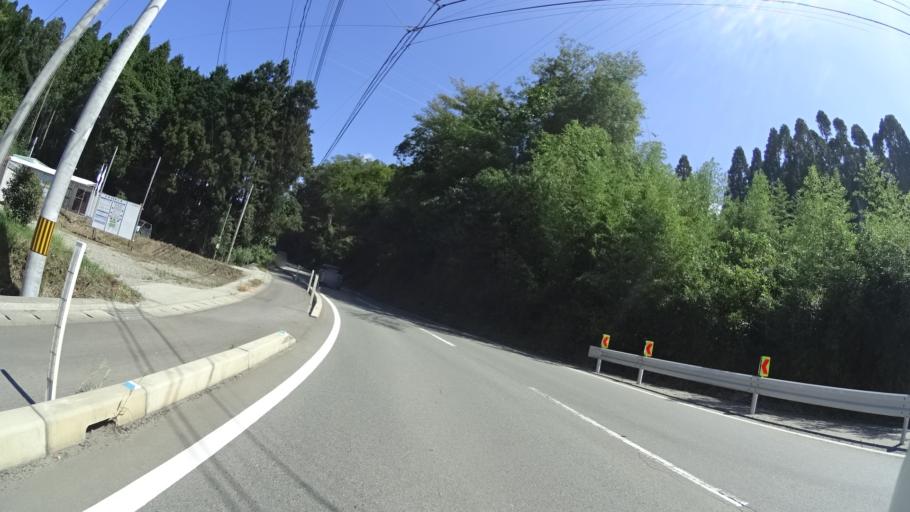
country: JP
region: Kumamoto
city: Aso
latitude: 32.8836
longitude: 130.9978
